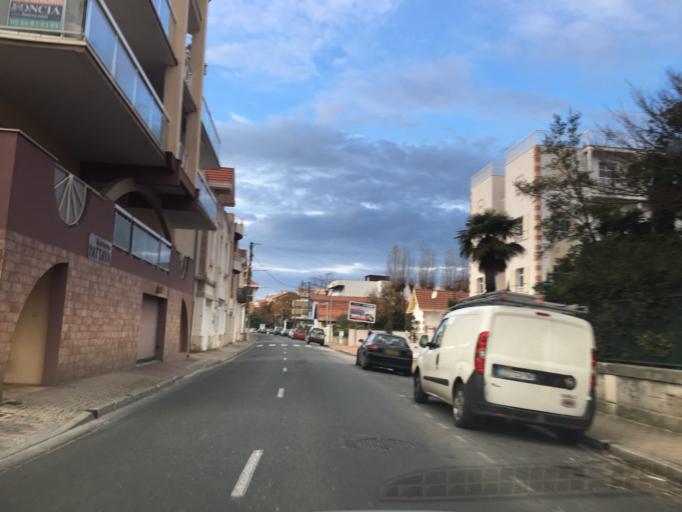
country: FR
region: Aquitaine
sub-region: Departement de la Gironde
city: Arcachon
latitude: 44.6616
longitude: -1.1570
